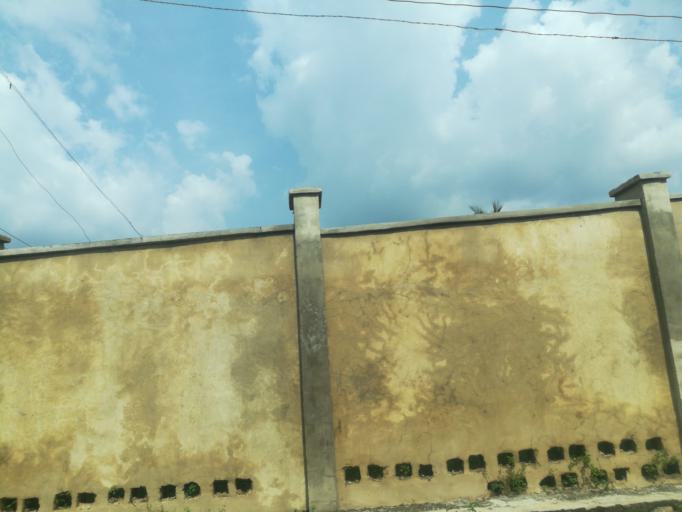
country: NG
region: Oyo
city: Moniya
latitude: 7.4627
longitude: 3.9194
